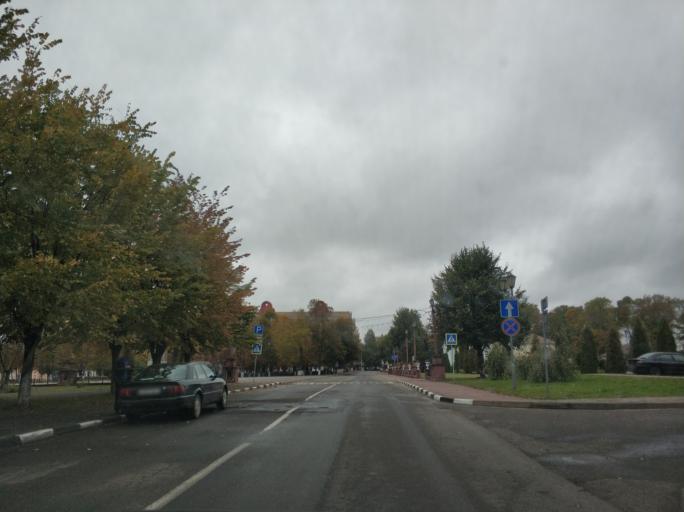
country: BY
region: Vitebsk
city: Polatsk
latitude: 55.4860
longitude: 28.7697
